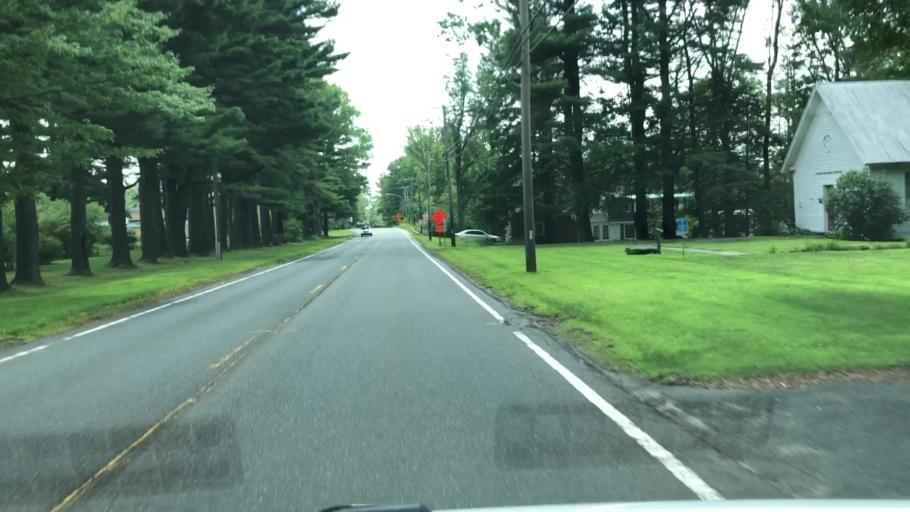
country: US
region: Massachusetts
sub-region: Hampshire County
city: Chesterfield
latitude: 42.4376
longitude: -72.7985
